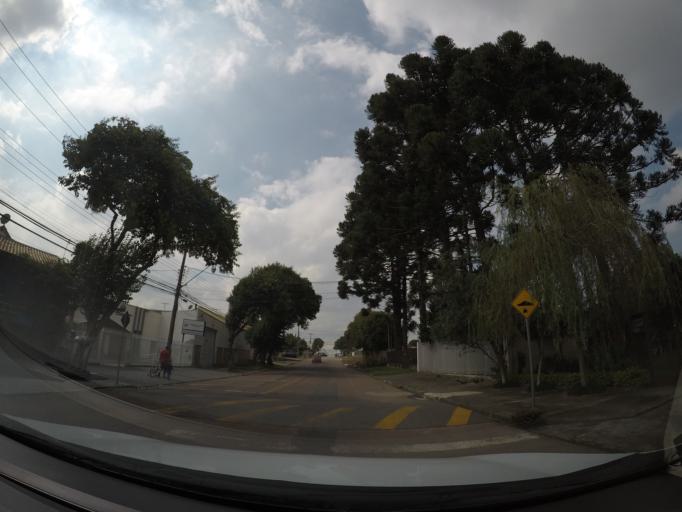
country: BR
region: Parana
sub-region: Sao Jose Dos Pinhais
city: Sao Jose dos Pinhais
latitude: -25.5030
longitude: -49.2476
